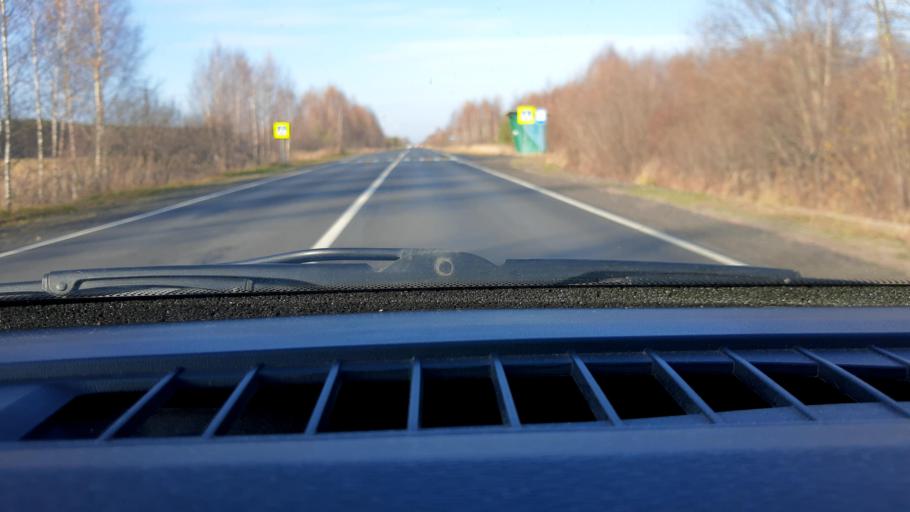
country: RU
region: Nizjnij Novgorod
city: Novaya Balakhna
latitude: 56.5909
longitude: 43.6610
